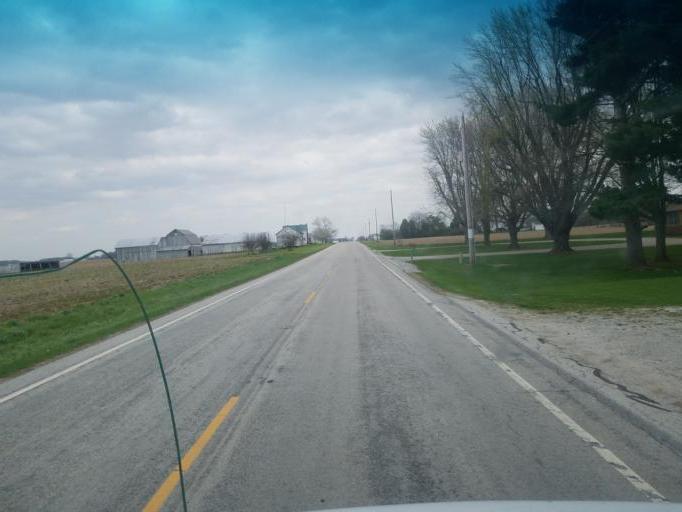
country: US
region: Ohio
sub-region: Seneca County
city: Tiffin
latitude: 40.9499
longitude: -83.1279
